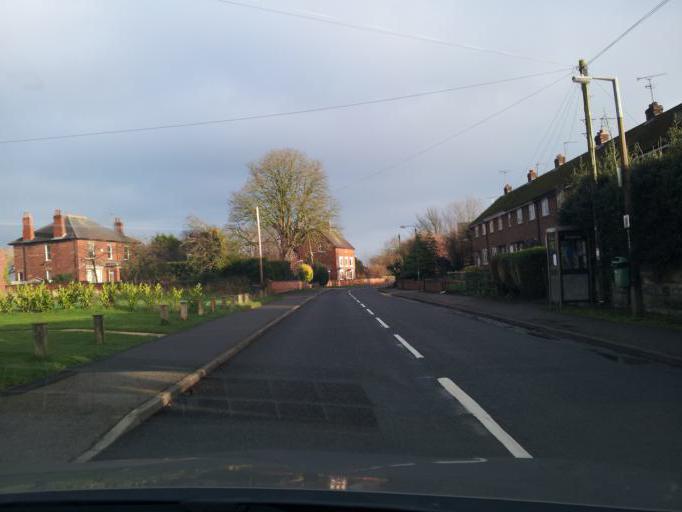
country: GB
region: England
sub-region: Derbyshire
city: Rodsley
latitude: 52.8689
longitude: -1.7133
